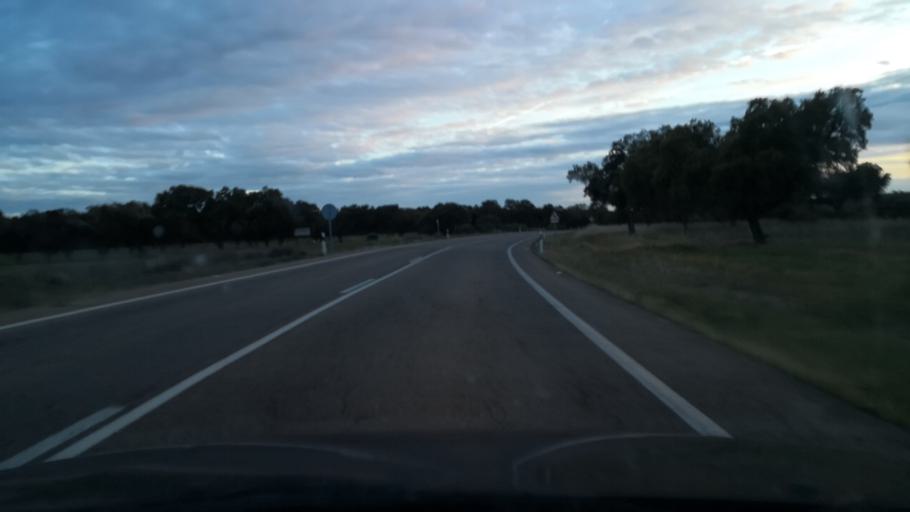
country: ES
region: Extremadura
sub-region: Provincia de Badajoz
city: Villar del Rey
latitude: 39.0412
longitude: -6.8098
